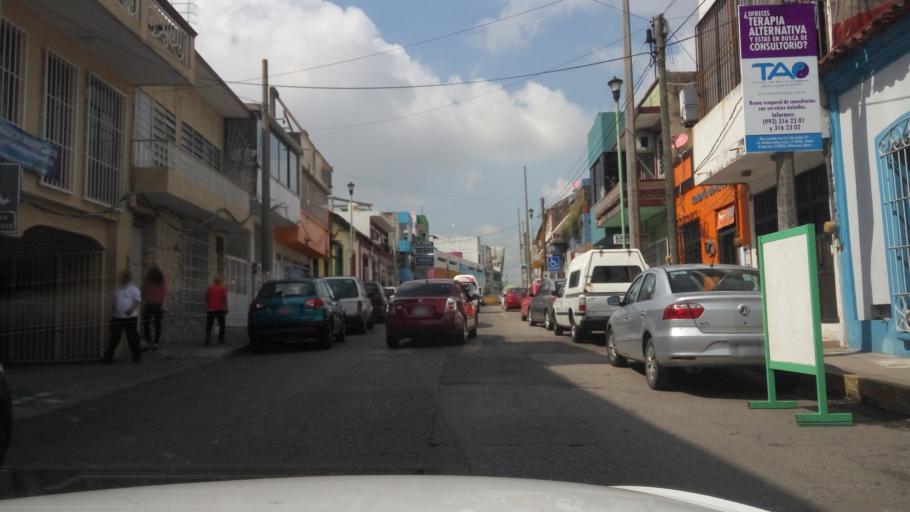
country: MX
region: Tabasco
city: Villahermosa
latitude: 17.9905
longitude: -92.9208
